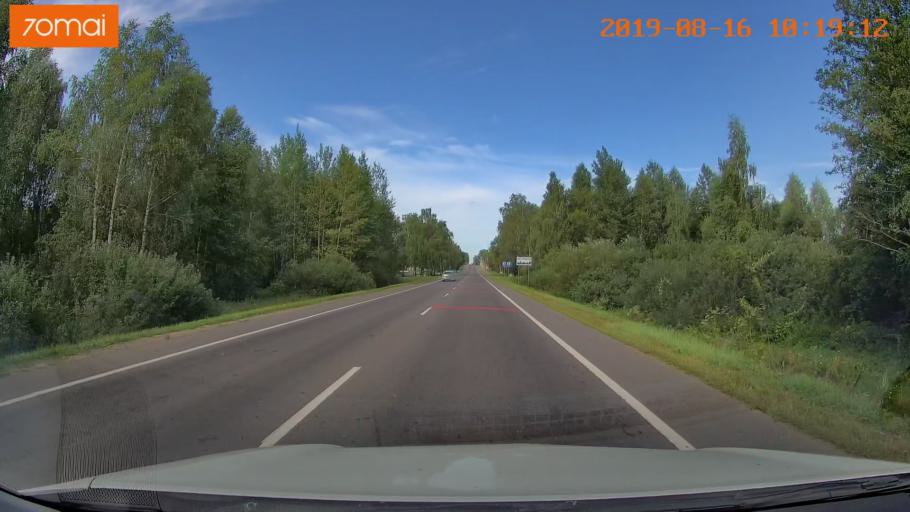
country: BY
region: Mogilev
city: Asipovichy
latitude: 53.3062
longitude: 28.6717
